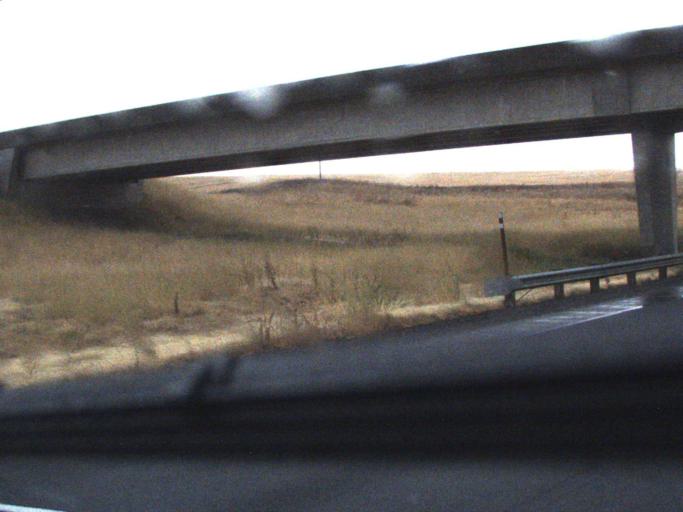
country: US
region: Washington
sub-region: Whitman County
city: Colfax
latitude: 47.2108
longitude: -117.3614
